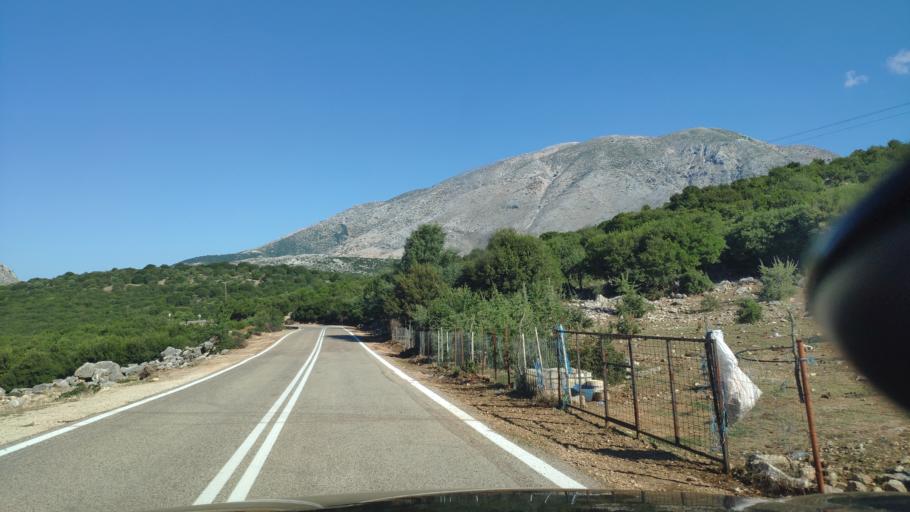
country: GR
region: West Greece
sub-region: Nomos Aitolias kai Akarnanias
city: Archontochorion
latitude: 38.6877
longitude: 21.0619
